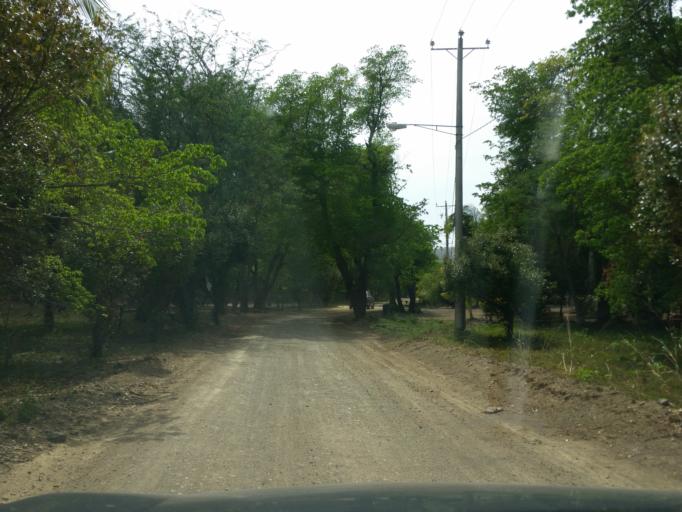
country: NI
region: Rivas
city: Tola
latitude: 11.4090
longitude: -86.0521
